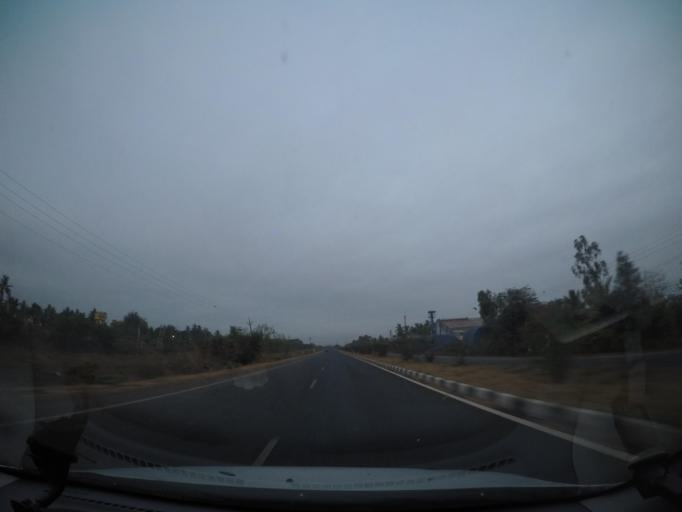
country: IN
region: Andhra Pradesh
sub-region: West Godavari
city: Tadepallegudem
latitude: 16.8082
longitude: 81.3175
